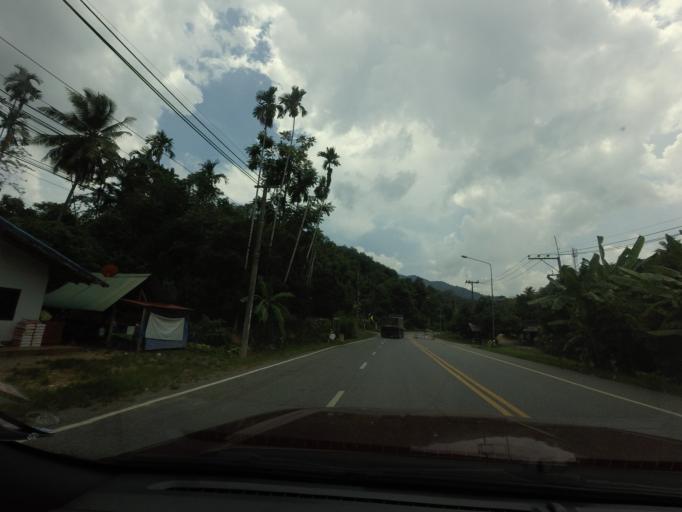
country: TH
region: Yala
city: Than To
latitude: 6.0761
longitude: 101.1902
